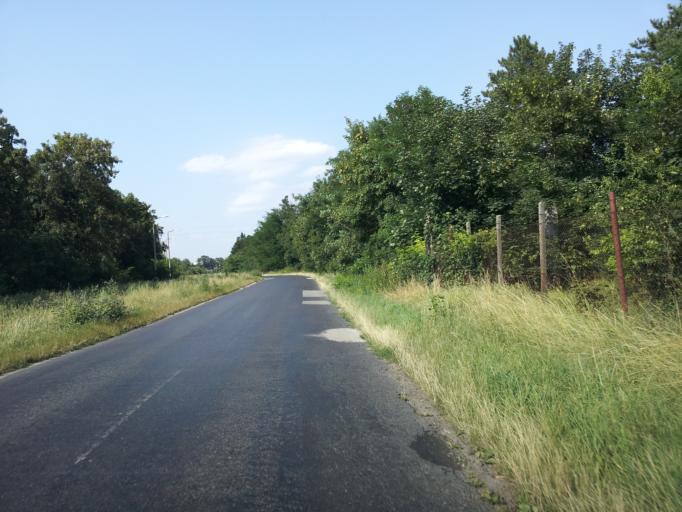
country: HU
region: Veszprem
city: Berhida
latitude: 47.1080
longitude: 18.0991
